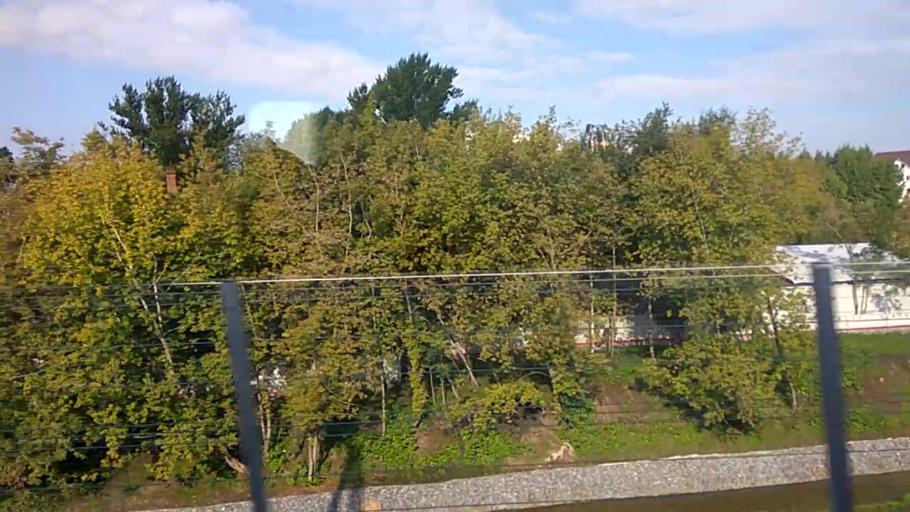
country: RU
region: Moscow
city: Tekstil'shchiki
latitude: 55.7271
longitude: 37.7242
